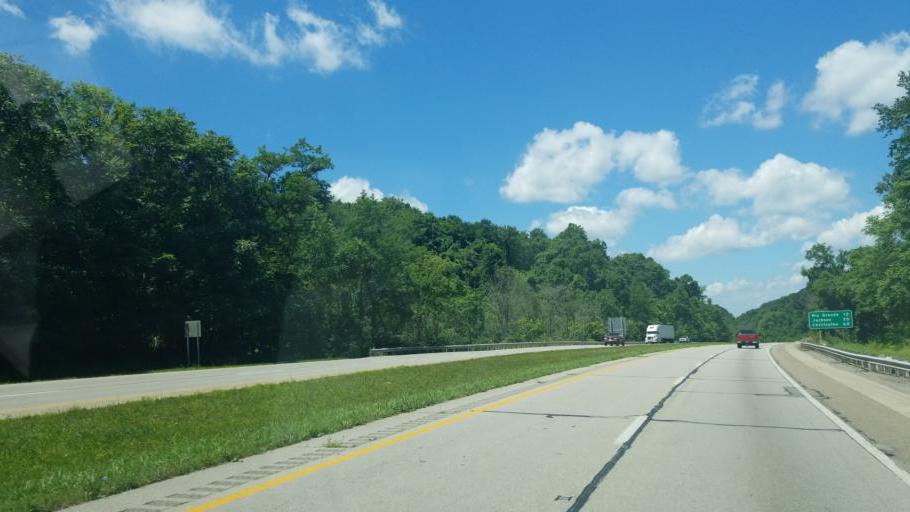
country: US
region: West Virginia
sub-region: Mason County
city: Point Pleasant
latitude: 38.8386
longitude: -82.1747
